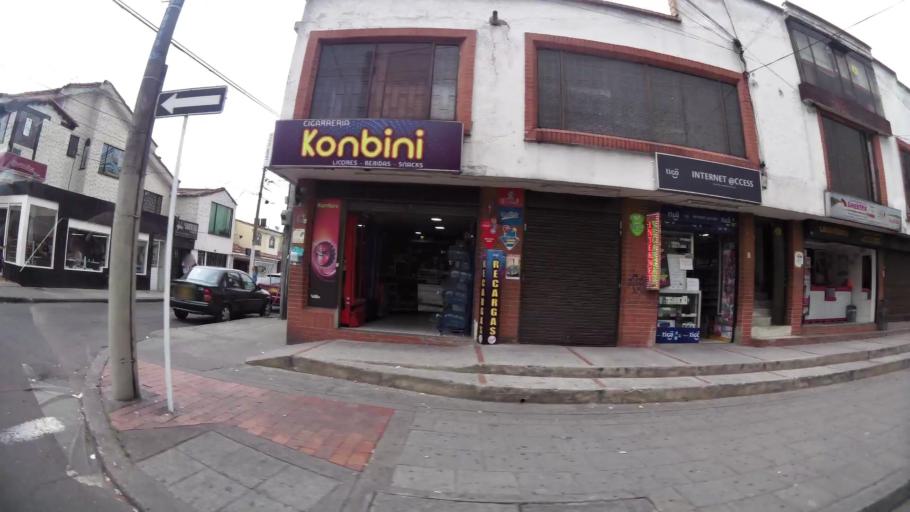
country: CO
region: Bogota D.C.
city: Bogota
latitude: 4.6665
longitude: -74.1194
